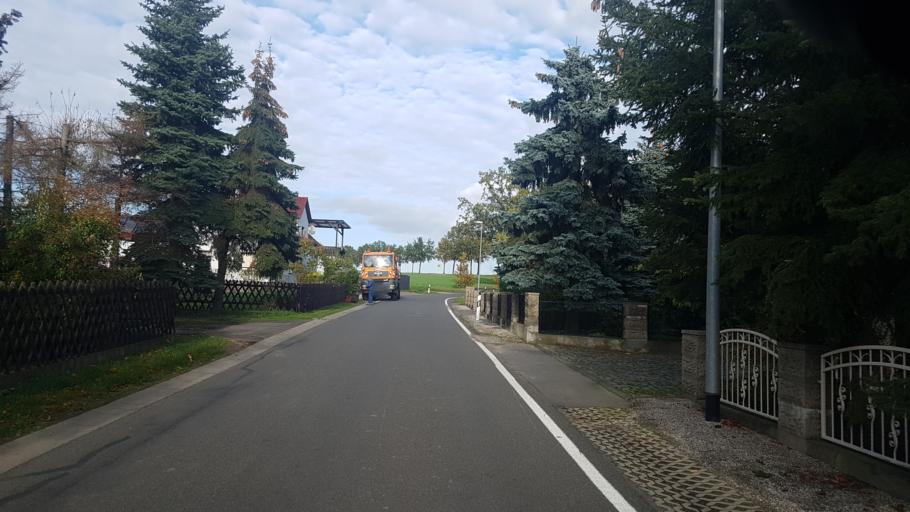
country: DE
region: Saxony
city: Dahlen
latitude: 51.3646
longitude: 13.0388
